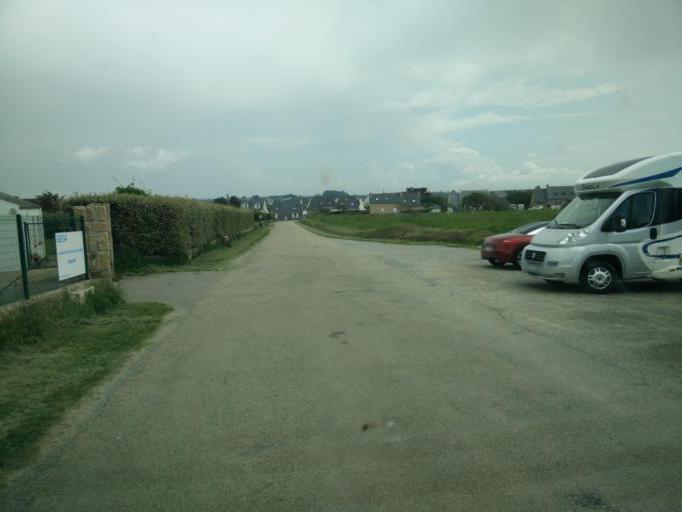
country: FR
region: Brittany
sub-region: Departement du Finistere
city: Camaret-sur-Mer
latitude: 48.2745
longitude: -4.6097
